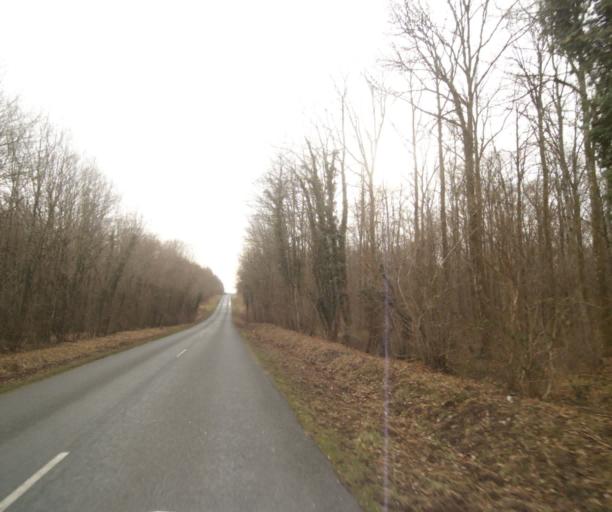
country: FR
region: Champagne-Ardenne
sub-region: Departement de la Haute-Marne
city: Villiers-en-Lieu
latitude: 48.7039
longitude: 4.8933
